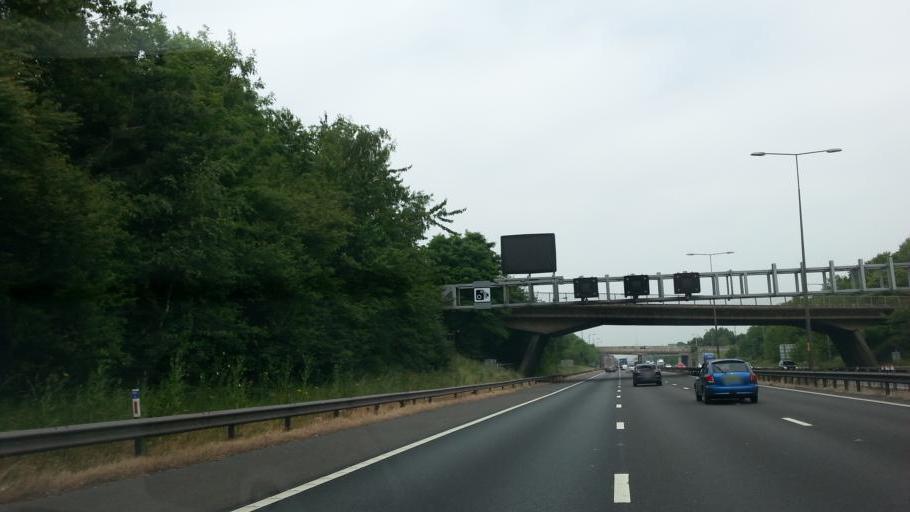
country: GB
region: England
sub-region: Staffordshire
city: Essington
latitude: 52.6336
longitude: -2.0514
